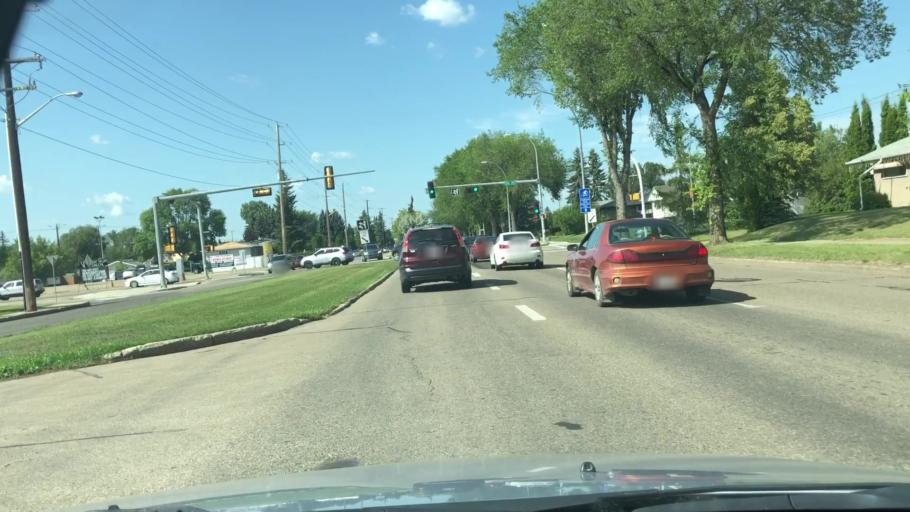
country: CA
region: Alberta
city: Edmonton
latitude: 53.5508
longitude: -113.4185
